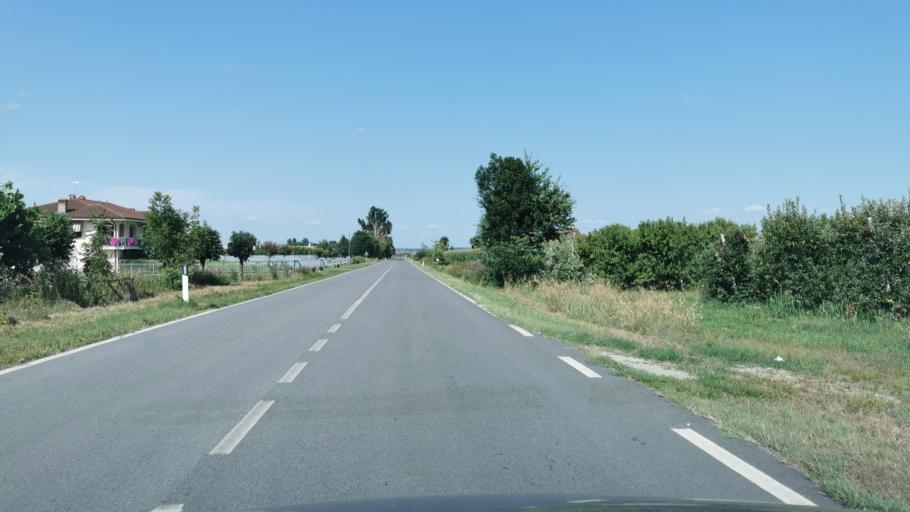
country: IT
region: Piedmont
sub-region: Provincia di Cuneo
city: Revello
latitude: 44.6735
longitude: 7.4039
